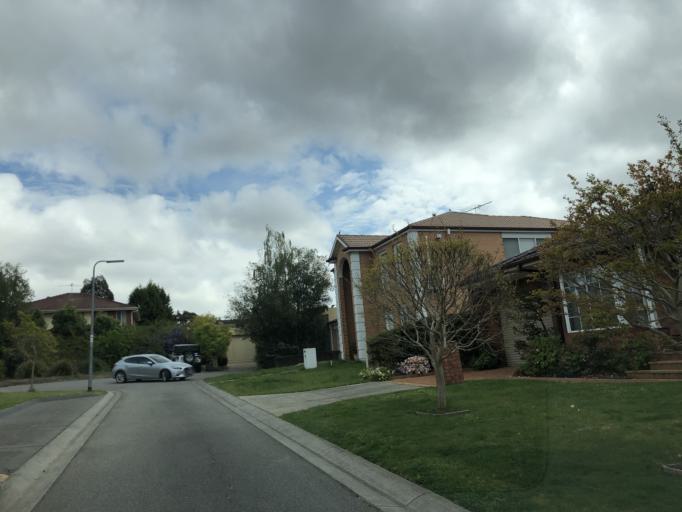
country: AU
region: Victoria
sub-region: Whitehorse
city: Blackburn South
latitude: -37.8432
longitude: 145.1580
